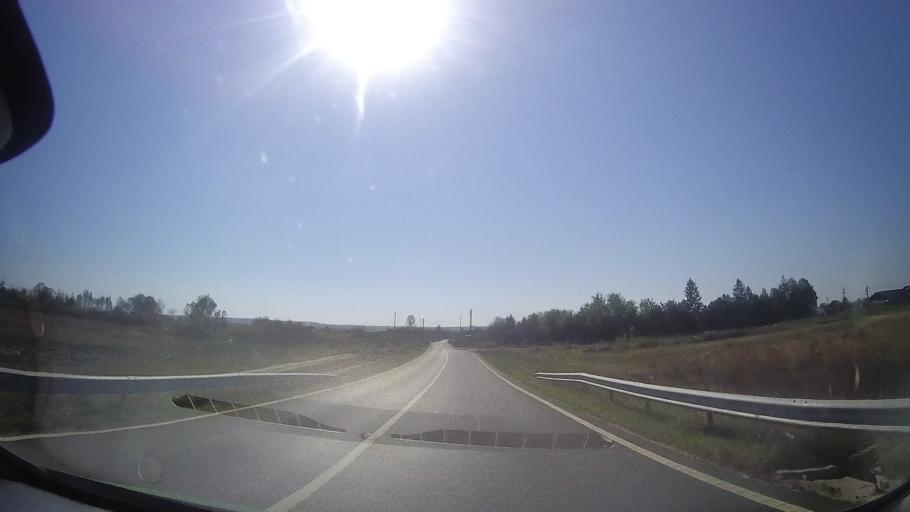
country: RO
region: Timis
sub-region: Comuna Bethausen
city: Bethausen
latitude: 45.8136
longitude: 21.9590
